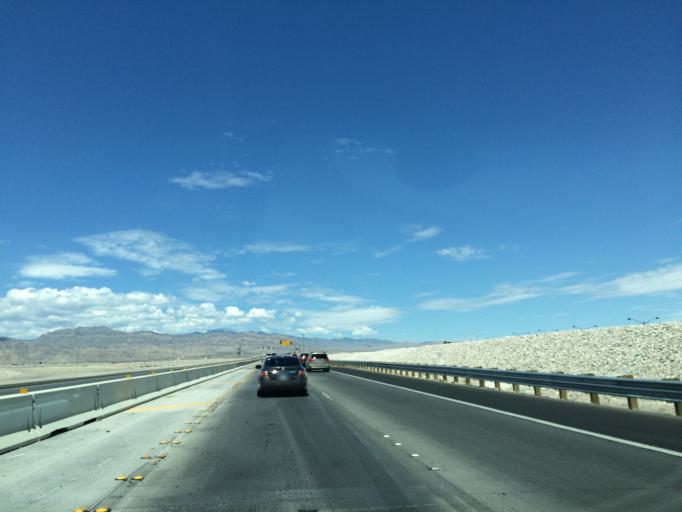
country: US
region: Nevada
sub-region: Clark County
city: Las Vegas
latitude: 36.2767
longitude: -115.2575
